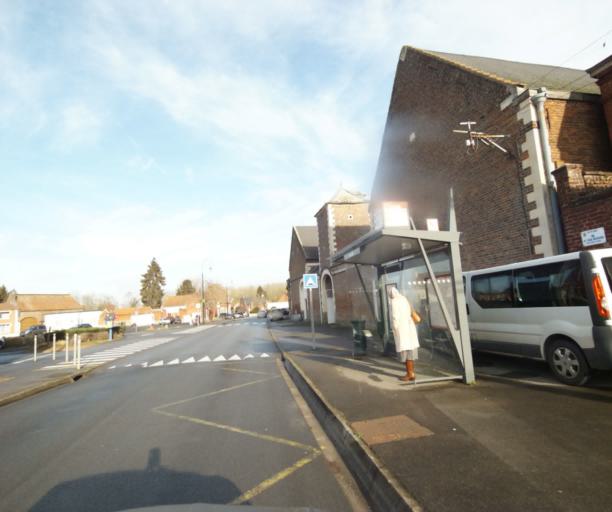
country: FR
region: Nord-Pas-de-Calais
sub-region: Departement du Nord
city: Maing
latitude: 50.3054
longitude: 3.4792
